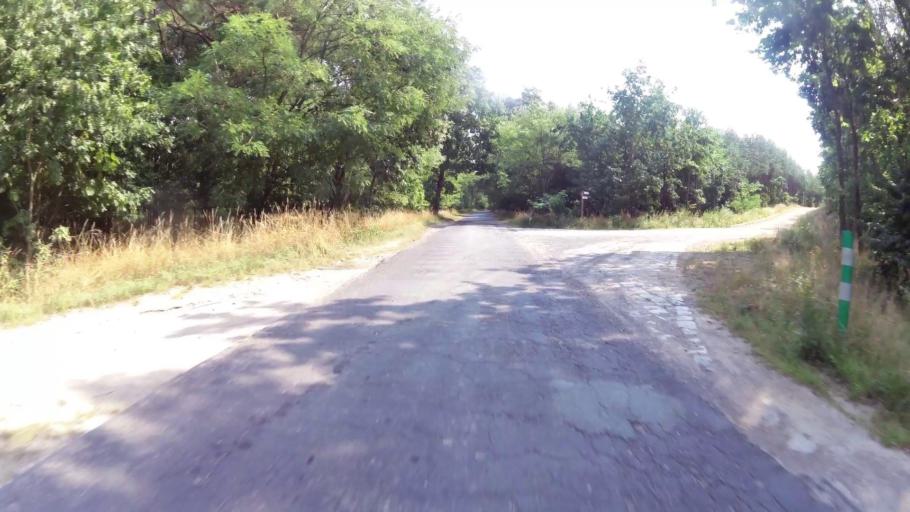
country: PL
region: West Pomeranian Voivodeship
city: Trzcinsko Zdroj
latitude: 52.8609
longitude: 14.6385
